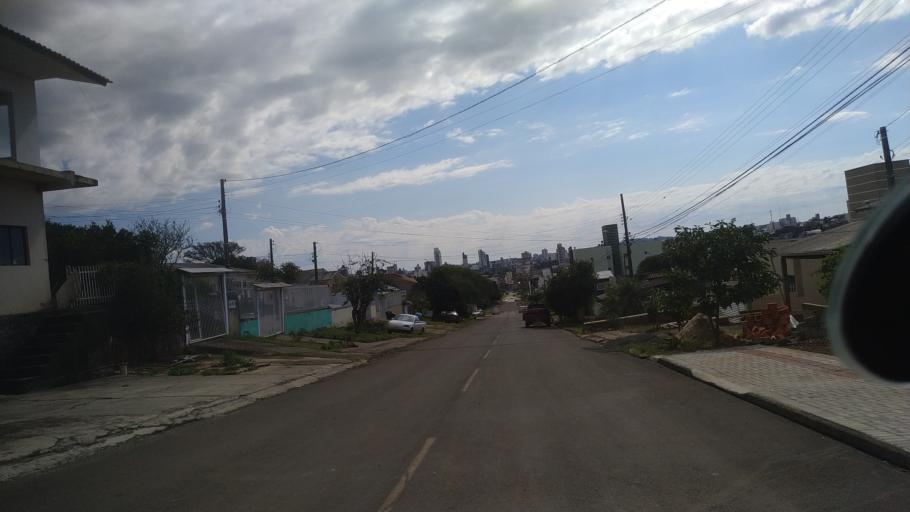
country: BR
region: Santa Catarina
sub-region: Chapeco
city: Chapeco
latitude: -27.1184
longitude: -52.6025
